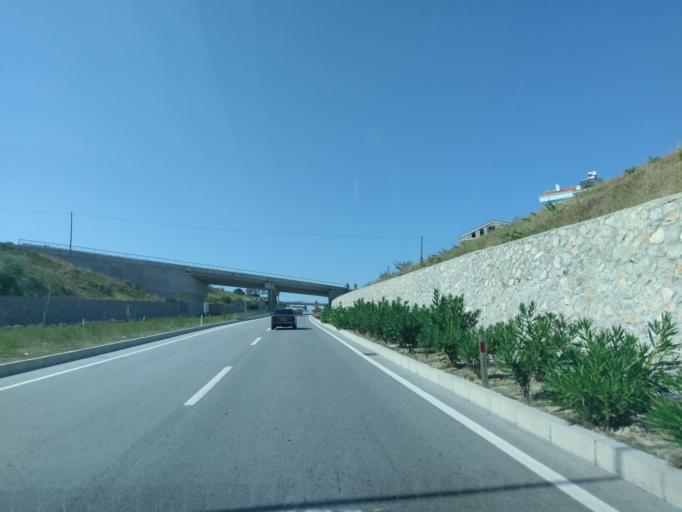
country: TR
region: Sinop
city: Gerze
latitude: 41.7912
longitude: 35.1892
